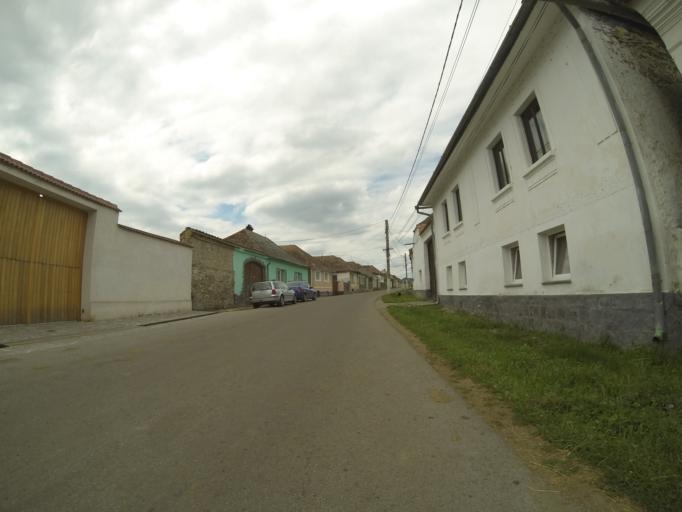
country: RO
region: Brasov
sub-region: Comuna Hoghiz
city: Hoghiz
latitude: 46.0252
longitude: 25.4017
